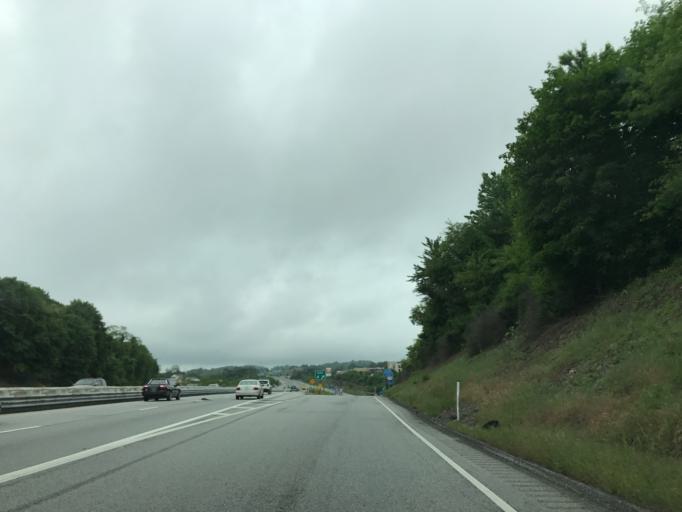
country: US
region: Pennsylvania
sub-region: York County
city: Shrewsbury
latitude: 39.7683
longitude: -76.6664
